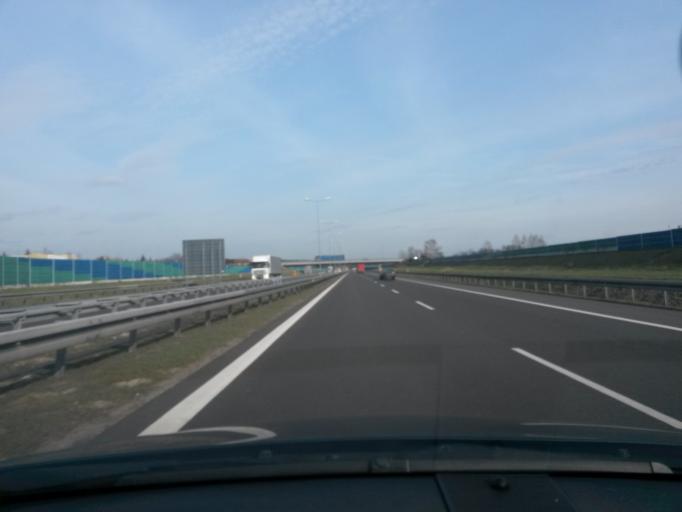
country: PL
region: Greater Poland Voivodeship
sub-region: Powiat wrzesinski
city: Wrzesnia
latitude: 52.3099
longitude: 17.5683
